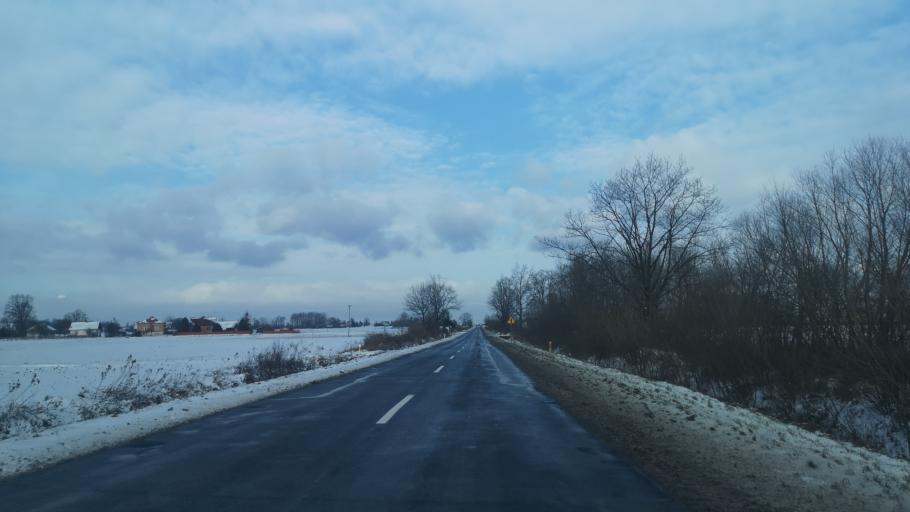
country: PL
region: Subcarpathian Voivodeship
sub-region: Powiat przeworski
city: Adamowka
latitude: 50.2231
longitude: 22.6518
